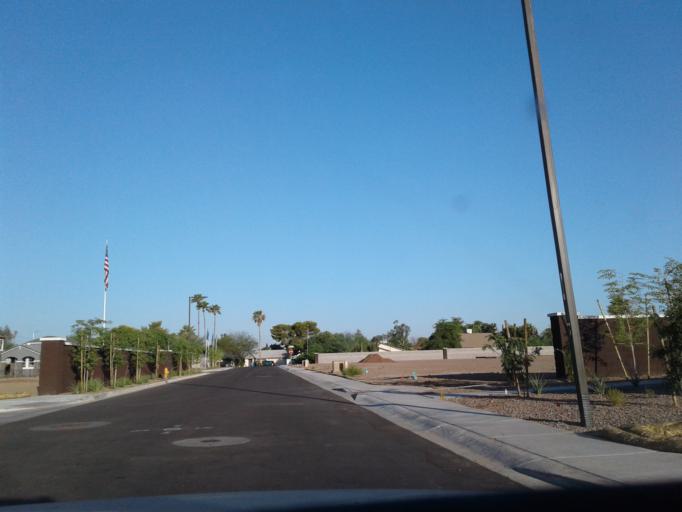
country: US
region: Arizona
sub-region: Maricopa County
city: Glendale
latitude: 33.6264
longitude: -112.1066
